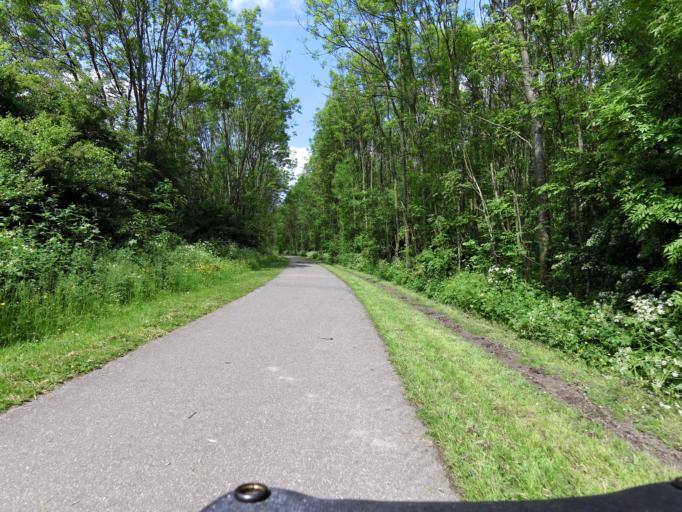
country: NL
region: South Holland
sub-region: Gemeente Spijkenisse
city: Spijkenisse
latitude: 51.8121
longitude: 4.2928
